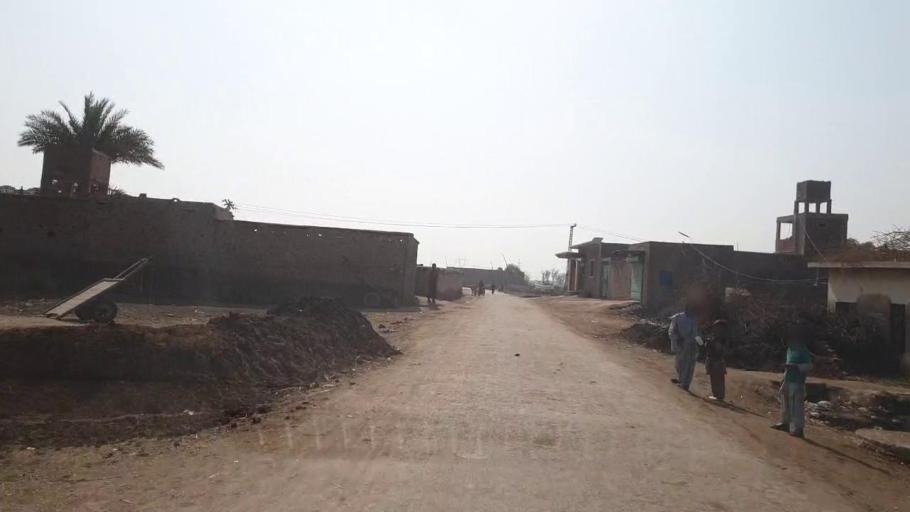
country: PK
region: Sindh
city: Bhit Shah
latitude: 25.7049
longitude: 68.5447
